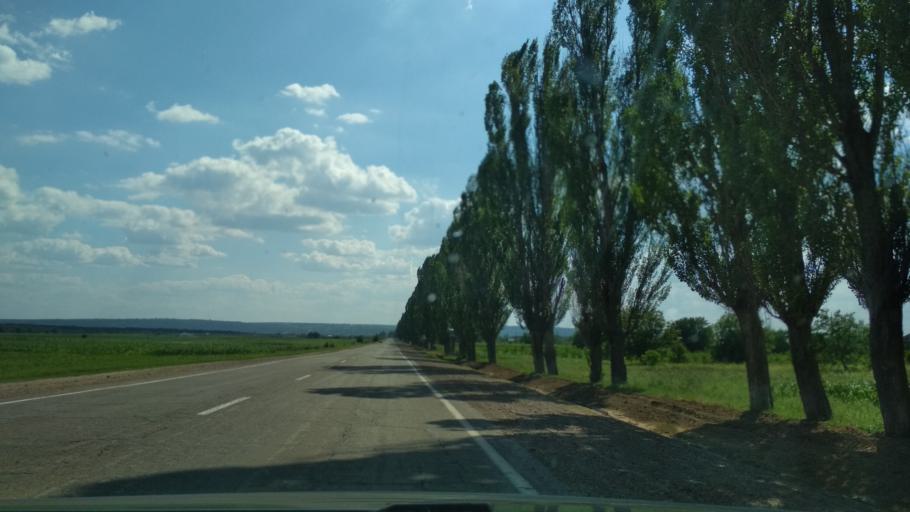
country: MD
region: Criuleni
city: Criuleni
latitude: 47.1412
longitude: 29.1391
